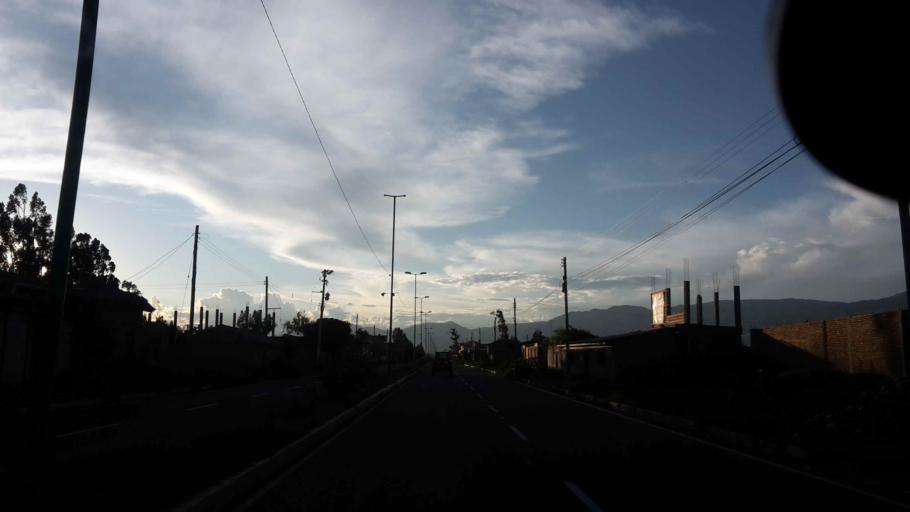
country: BO
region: Cochabamba
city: Arani
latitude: -17.5608
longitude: -65.7989
